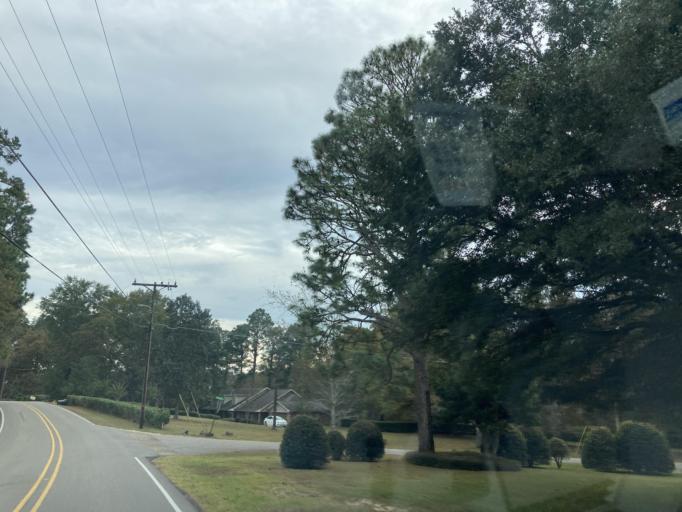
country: US
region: Mississippi
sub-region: Lamar County
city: West Hattiesburg
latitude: 31.3110
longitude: -89.4390
